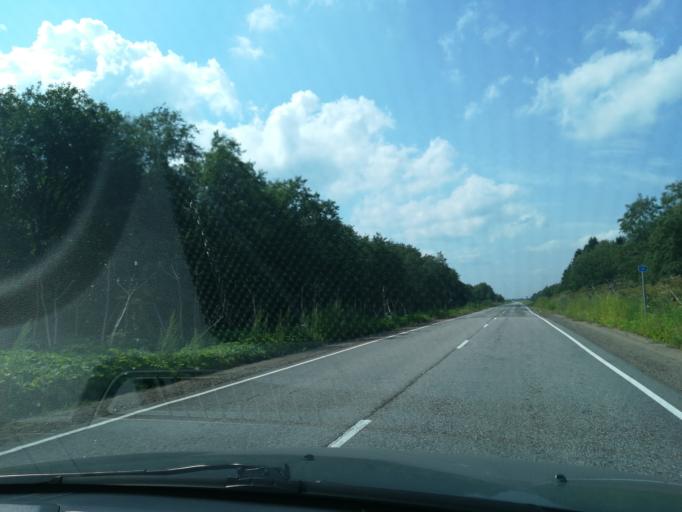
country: RU
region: Leningrad
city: Kopor'ye
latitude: 59.6887
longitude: 29.0467
